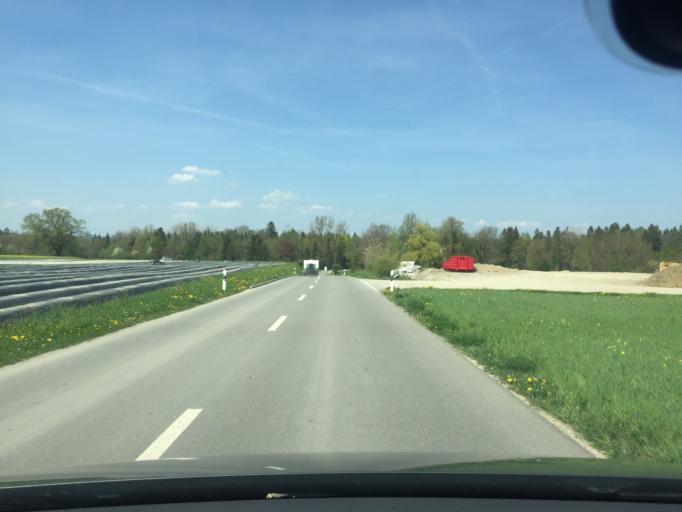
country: CH
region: Zurich
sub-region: Bezirk Buelach
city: Freienstein
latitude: 47.5871
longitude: 8.6059
